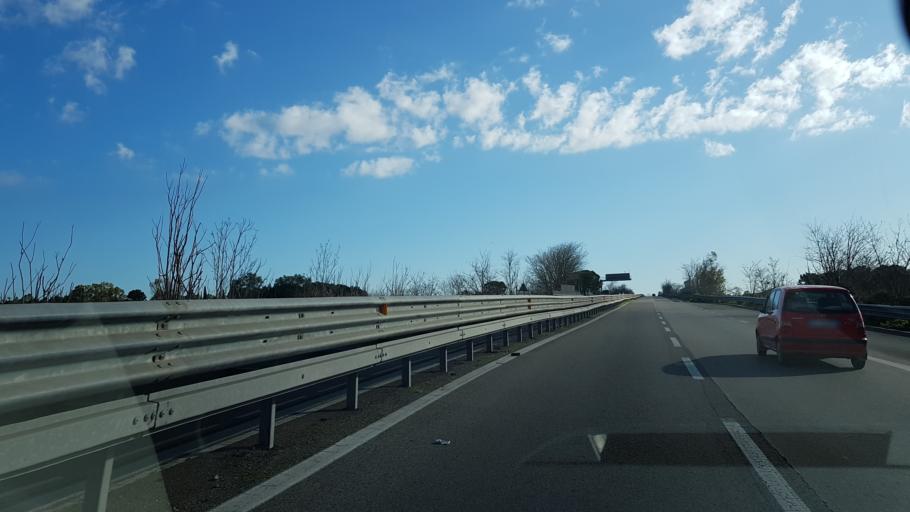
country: IT
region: Apulia
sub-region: Provincia di Lecce
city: Castromediano
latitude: 40.3258
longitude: 18.1631
